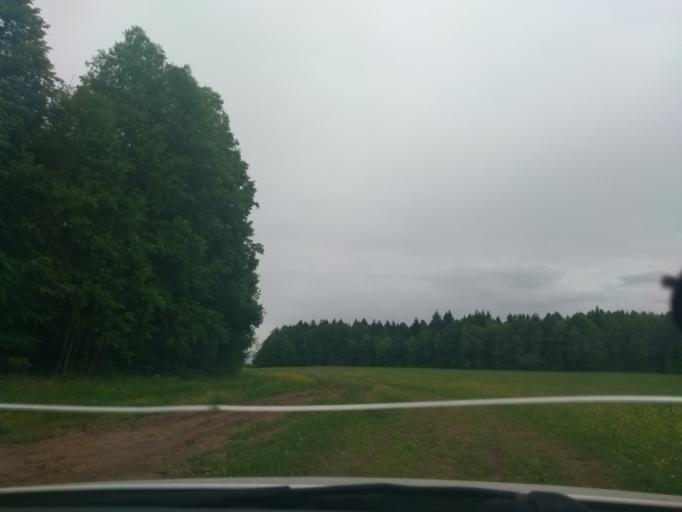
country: RU
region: Perm
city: Froly
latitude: 57.9833
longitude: 56.3316
